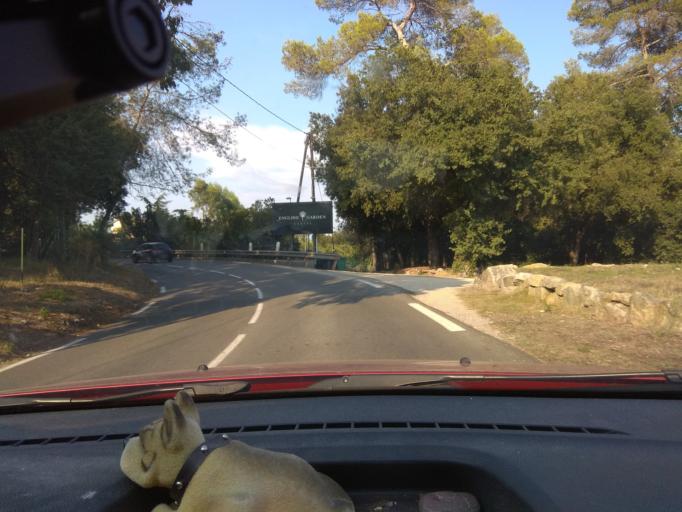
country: FR
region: Provence-Alpes-Cote d'Azur
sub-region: Departement des Alpes-Maritimes
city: Le Rouret
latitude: 43.6523
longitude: 7.0285
